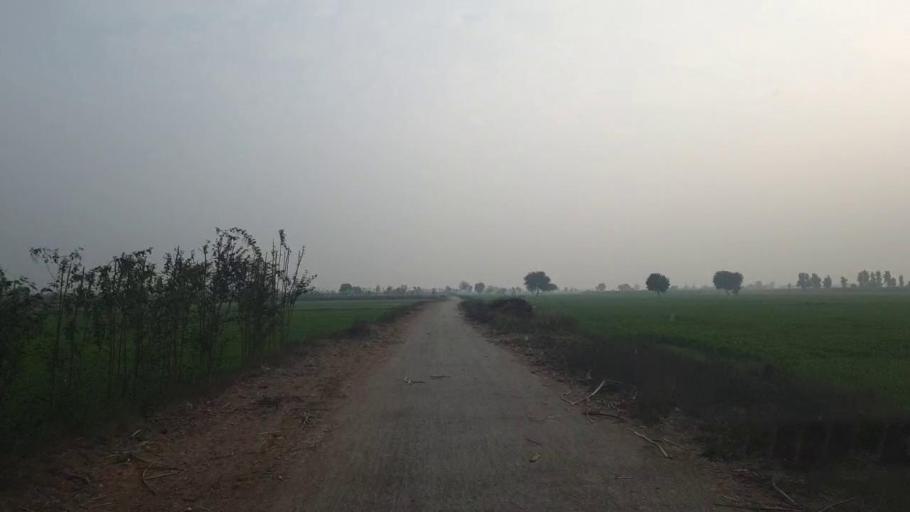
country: PK
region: Sindh
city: Berani
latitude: 25.7993
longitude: 68.7467
